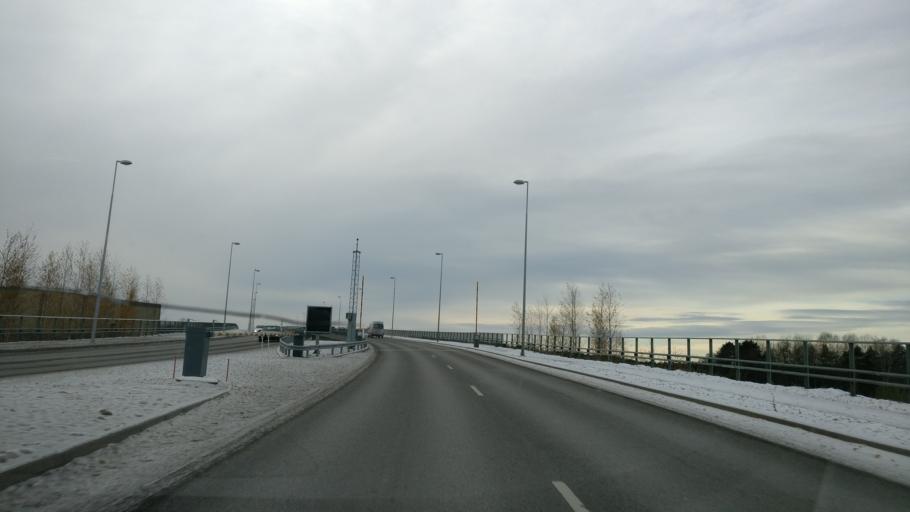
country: FI
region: Southern Savonia
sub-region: Savonlinna
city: Savonlinna
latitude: 61.8706
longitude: 28.9138
